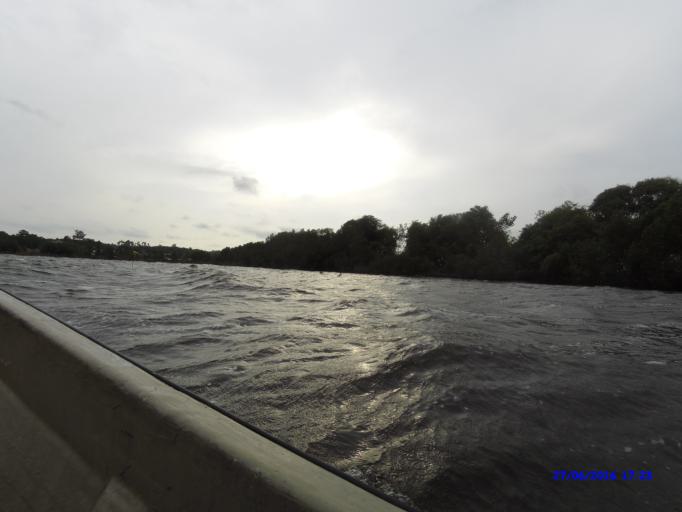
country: BJ
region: Atlantique
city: Allada
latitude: 6.6023
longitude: 1.9811
